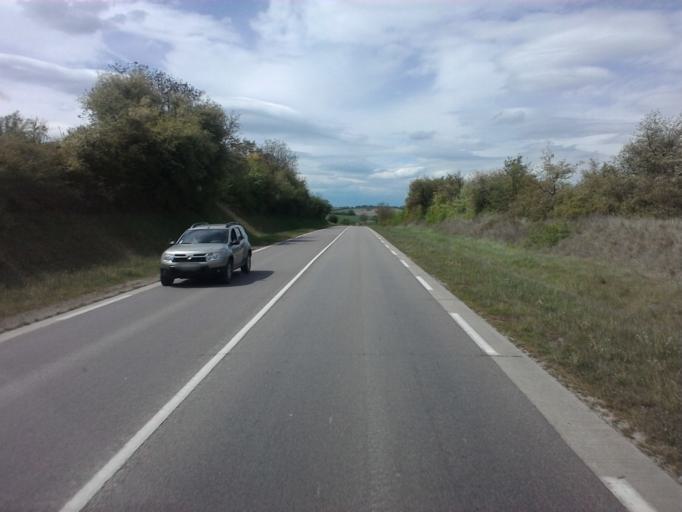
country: FR
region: Bourgogne
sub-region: Departement de l'Yonne
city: Saint-Bris-le-Vineux
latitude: 47.6963
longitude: 3.6357
